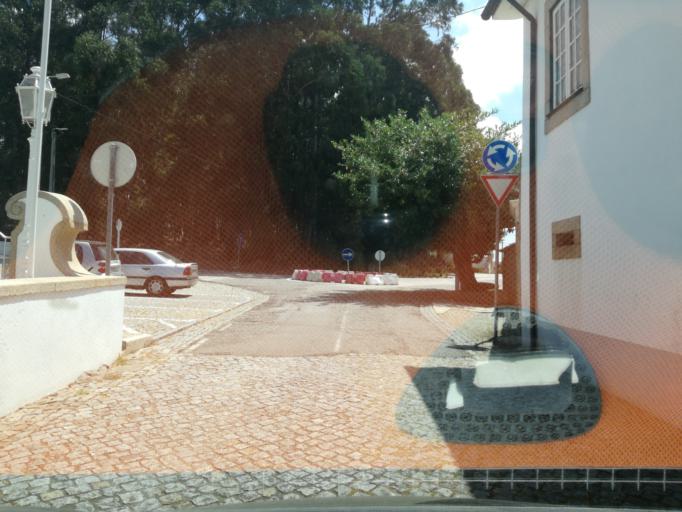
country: PT
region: Porto
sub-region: Maia
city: Maia
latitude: 41.2460
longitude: -8.6128
